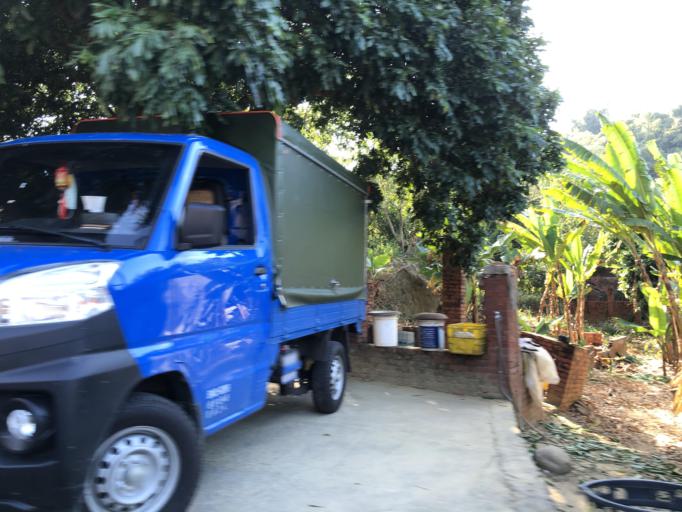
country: TW
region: Taiwan
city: Yujing
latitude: 23.0144
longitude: 120.3853
